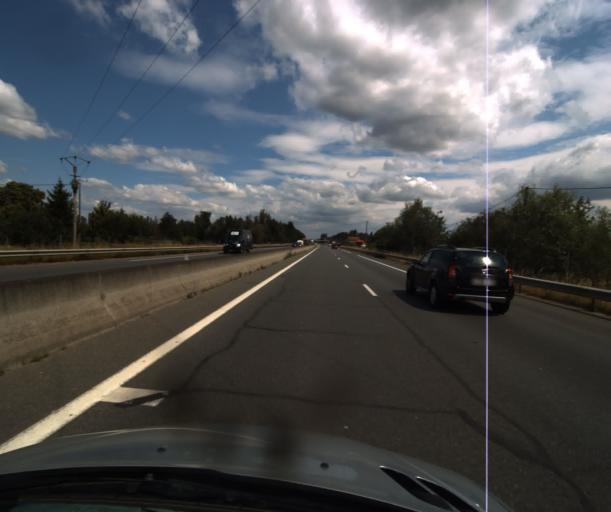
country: FR
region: Midi-Pyrenees
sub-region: Departement du Tarn-et-Garonne
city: Bressols
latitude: 43.9712
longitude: 1.3320
